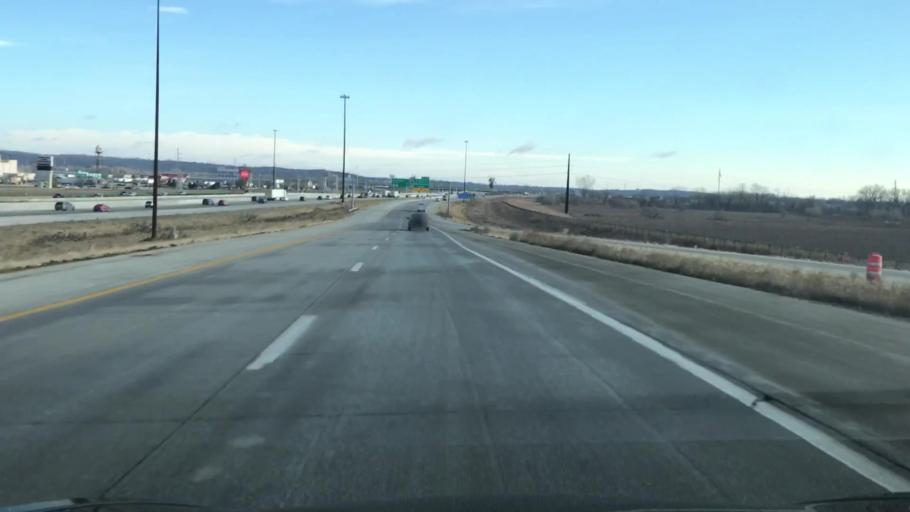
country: US
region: Iowa
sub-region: Pottawattamie County
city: Council Bluffs
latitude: 41.2318
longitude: -95.8940
